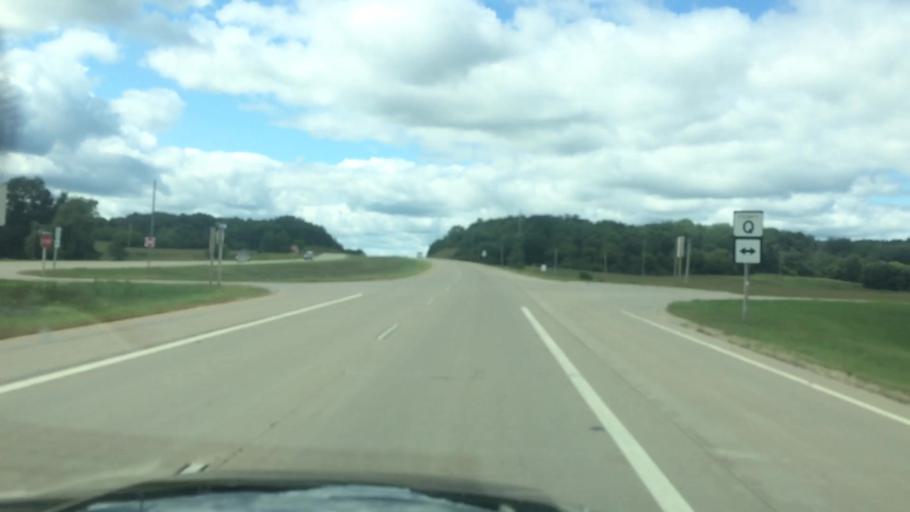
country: US
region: Wisconsin
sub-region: Waupaca County
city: King
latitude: 44.3837
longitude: -89.1791
